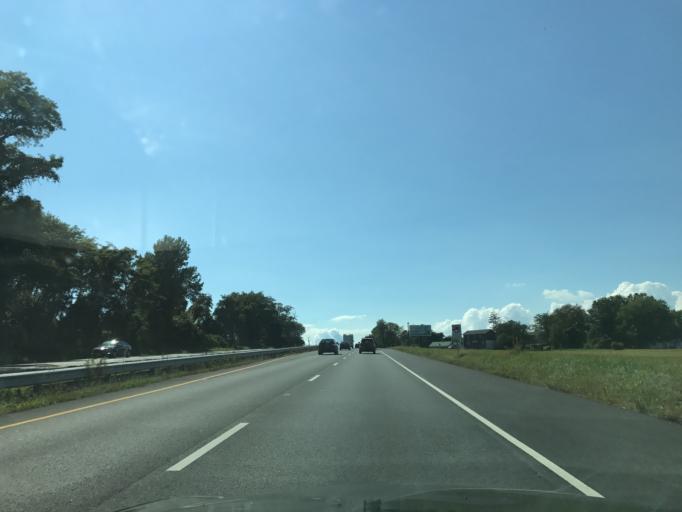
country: US
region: Maryland
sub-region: Cecil County
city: Perryville
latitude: 39.5805
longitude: -76.0328
